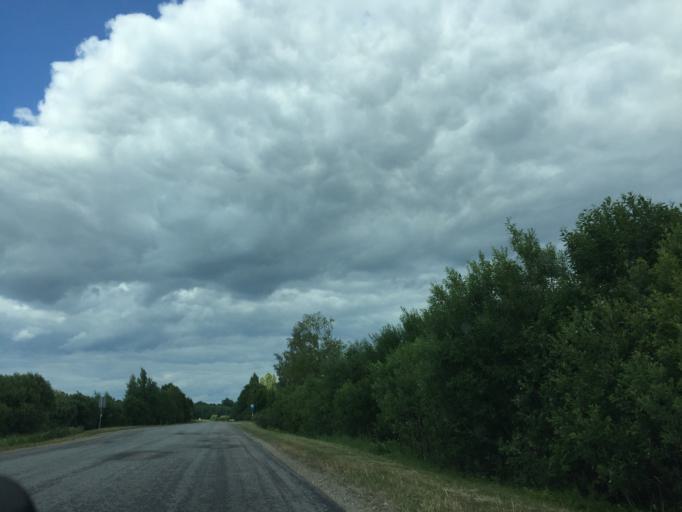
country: LV
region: Skriveri
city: Skriveri
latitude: 56.8215
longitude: 25.1209
